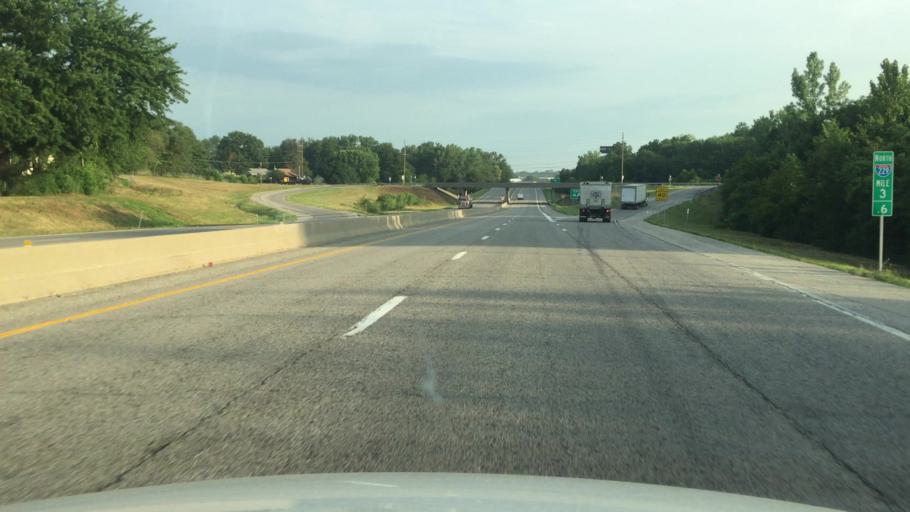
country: US
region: Kansas
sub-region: Doniphan County
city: Elwood
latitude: 39.7314
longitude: -94.8470
